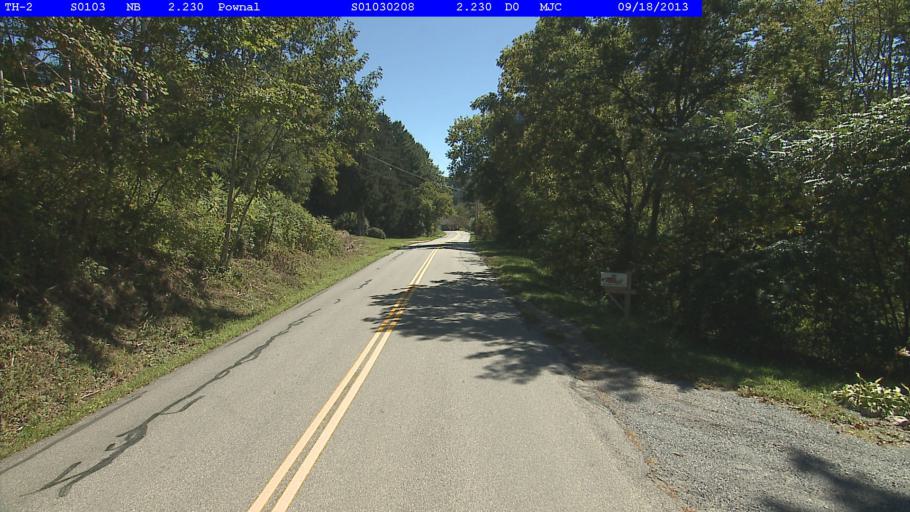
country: US
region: Vermont
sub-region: Bennington County
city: Bennington
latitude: 42.7991
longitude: -73.2337
